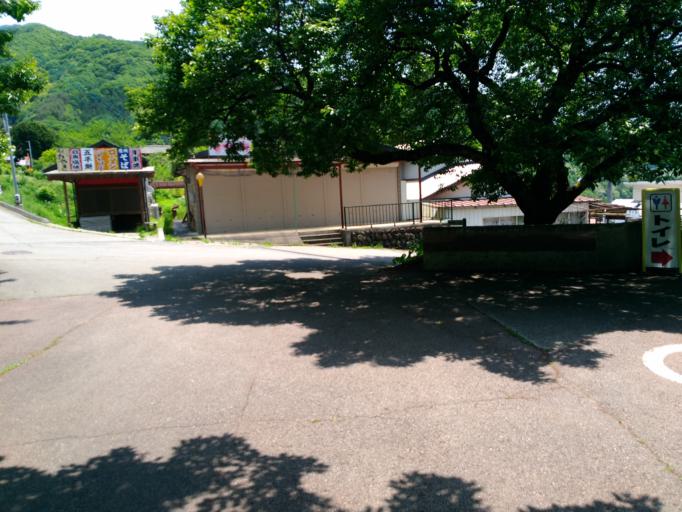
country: JP
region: Nagano
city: Ina
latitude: 35.8320
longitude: 138.0634
